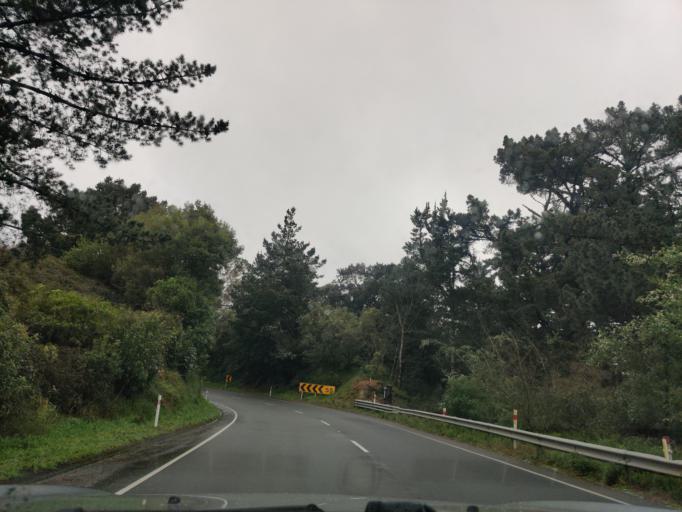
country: NZ
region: Manawatu-Wanganui
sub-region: Palmerston North City
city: Palmerston North
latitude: -40.0526
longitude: 176.2445
